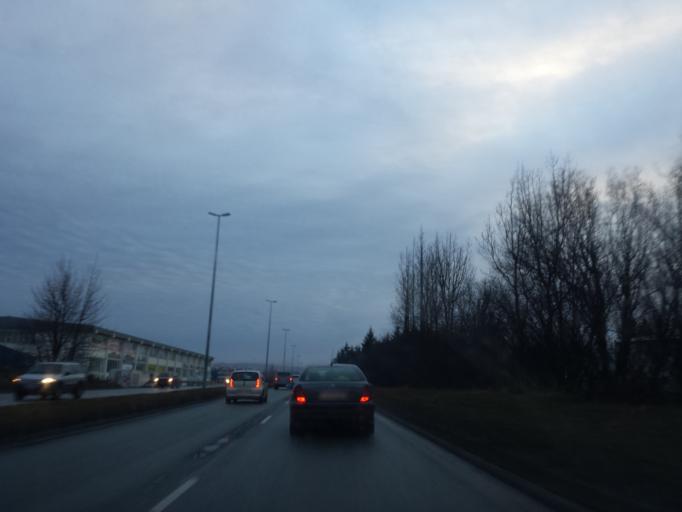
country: IS
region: Capital Region
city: Reykjavik
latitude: 64.1332
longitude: -21.8500
